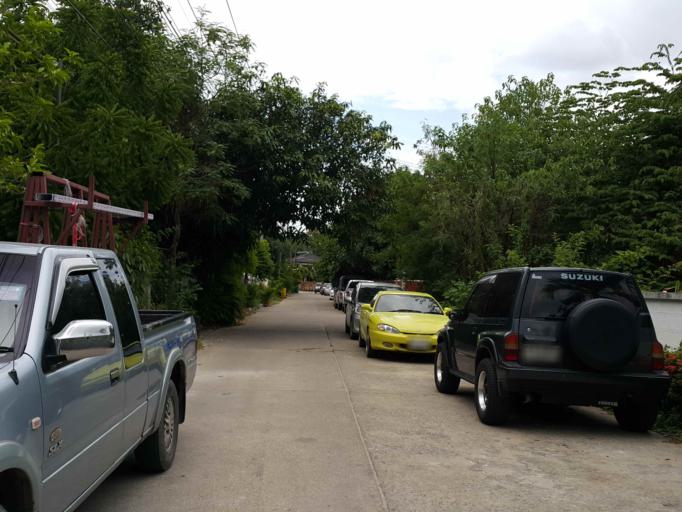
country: TH
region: Chiang Mai
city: Chiang Mai
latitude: 18.7660
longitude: 99.0224
